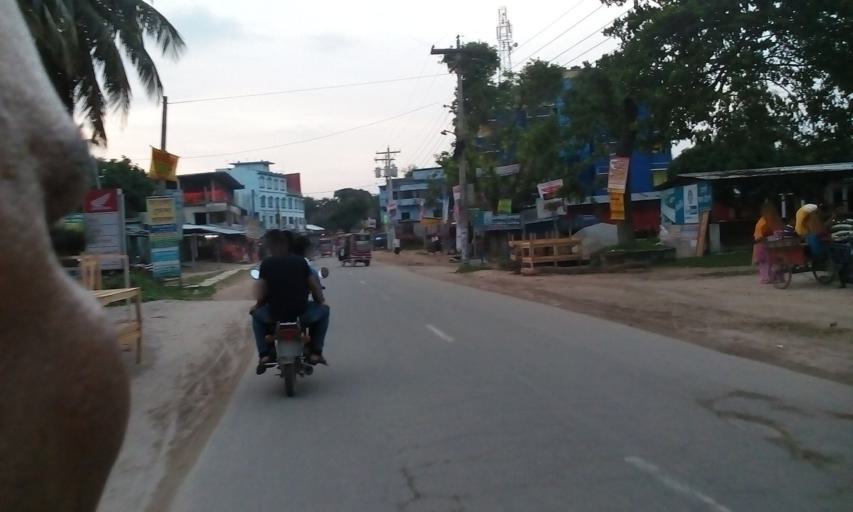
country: IN
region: West Bengal
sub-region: Dakshin Dinajpur
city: Balurghat
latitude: 25.3851
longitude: 88.9881
